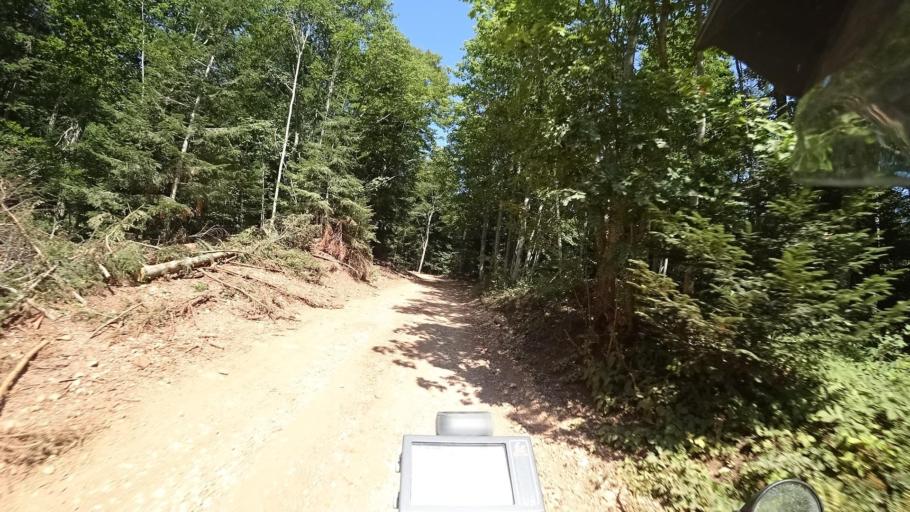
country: HR
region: Licko-Senjska
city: Popovaca
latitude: 44.5719
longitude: 15.2005
